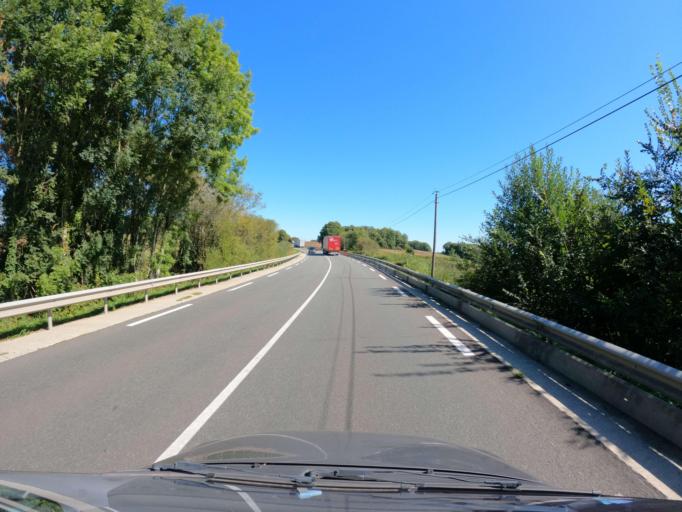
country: FR
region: Limousin
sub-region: Departement de la Haute-Vienne
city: Arnac-la-Poste
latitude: 46.1997
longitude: 1.3638
